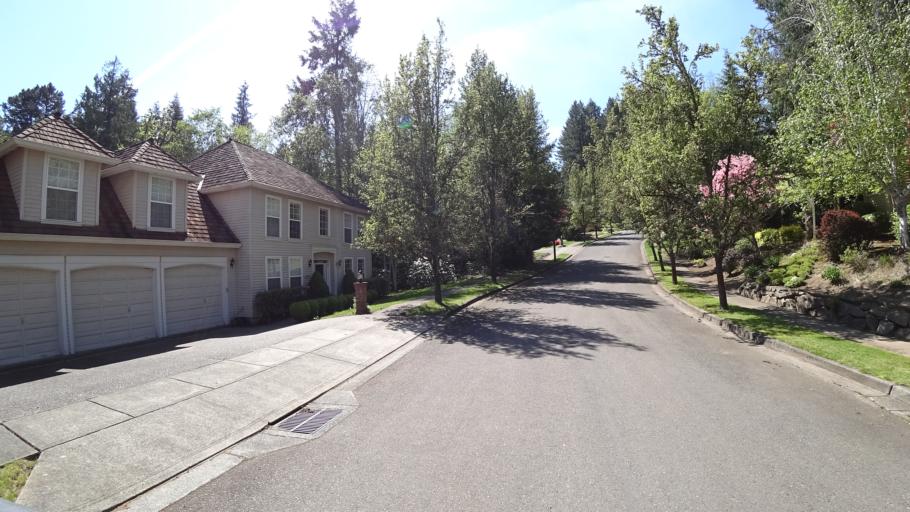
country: US
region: Oregon
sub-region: Washington County
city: Aloha
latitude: 45.4439
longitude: -122.8448
